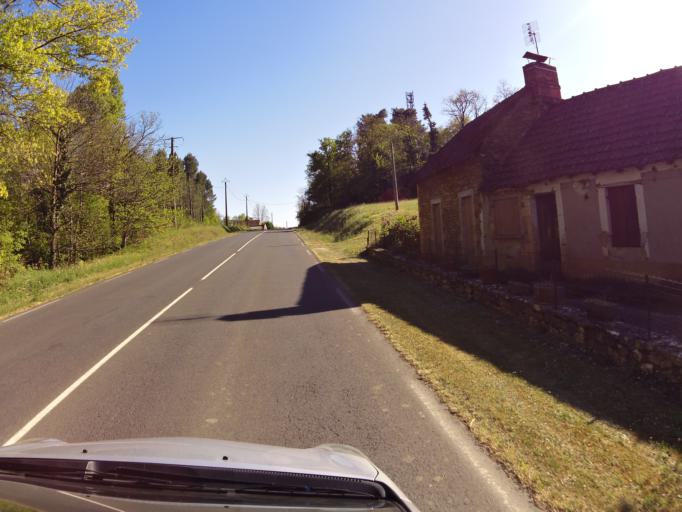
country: FR
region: Aquitaine
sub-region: Departement de la Dordogne
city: Montignac
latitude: 44.9930
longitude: 1.2417
